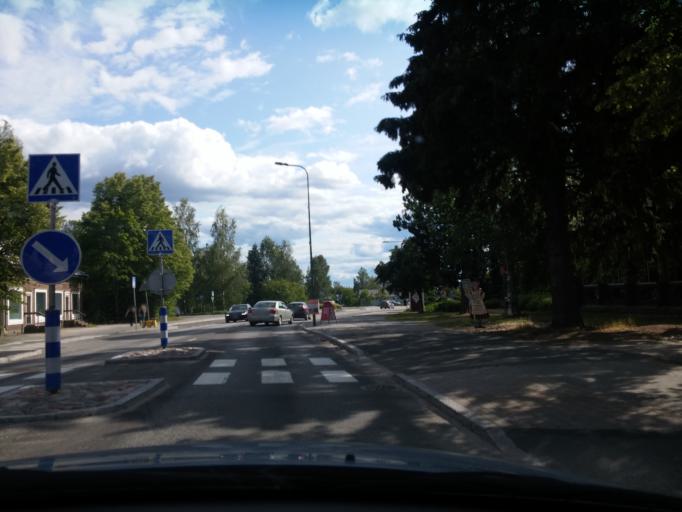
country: FI
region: Central Finland
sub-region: Keuruu
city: Keuruu
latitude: 62.2573
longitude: 24.7083
